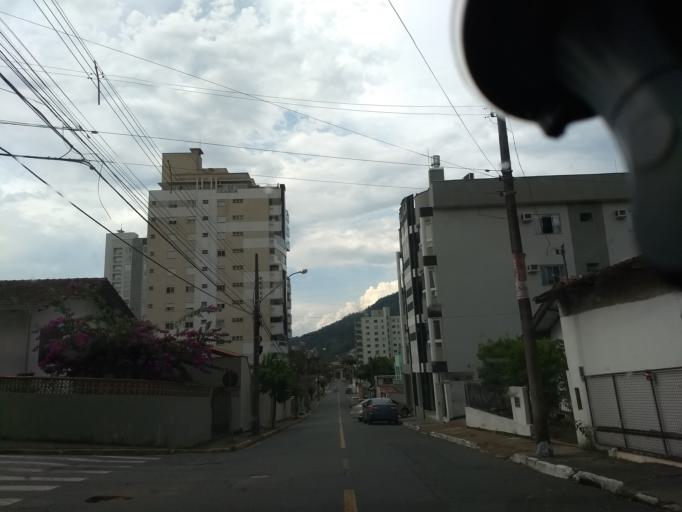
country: BR
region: Santa Catarina
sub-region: Jaragua Do Sul
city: Jaragua do Sul
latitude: -26.4823
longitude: -49.0878
